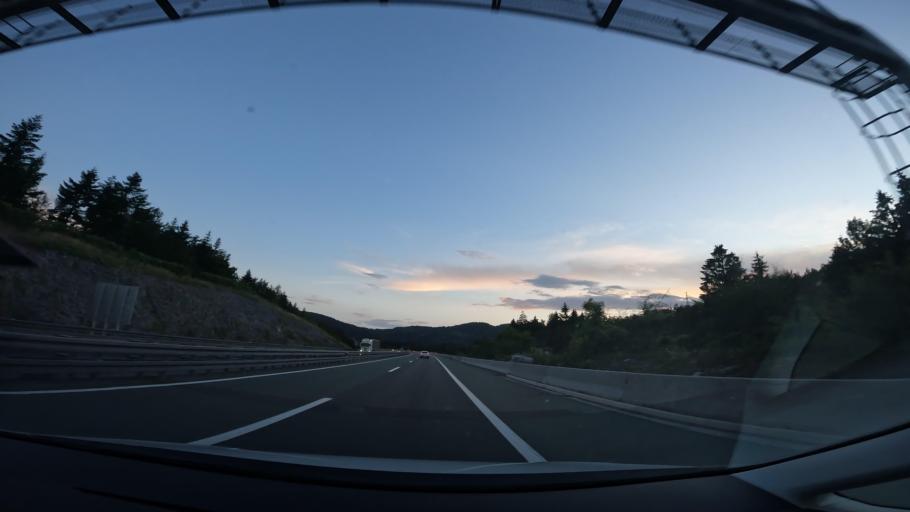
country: HR
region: Primorsko-Goranska
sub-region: Grad Delnice
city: Delnice
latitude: 45.3634
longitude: 14.7605
